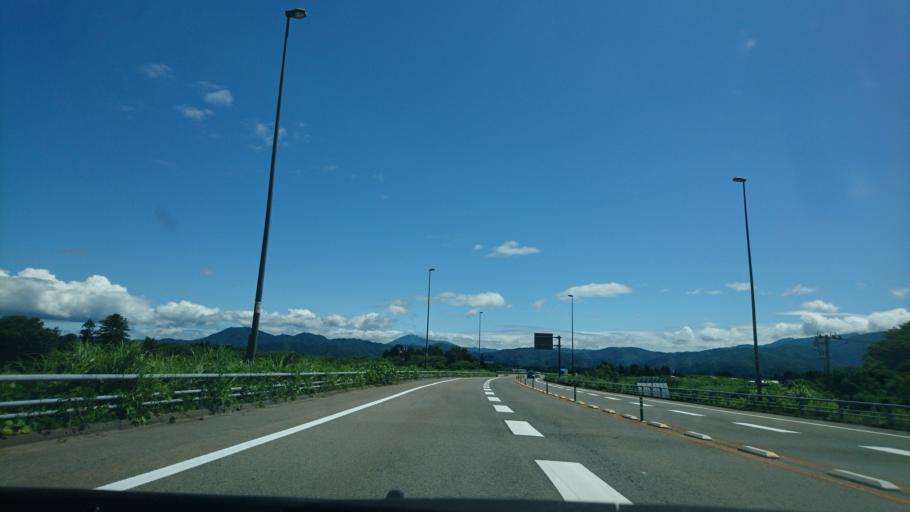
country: JP
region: Akita
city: Kakunodatemachi
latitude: 39.6105
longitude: 140.5589
